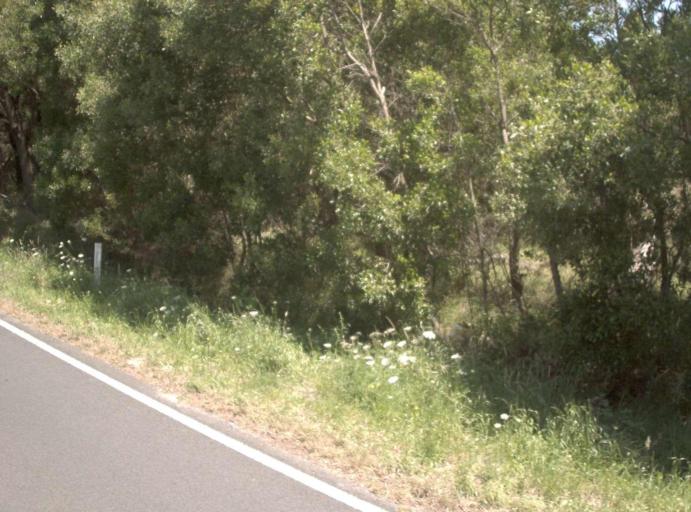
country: AU
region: Victoria
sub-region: Bass Coast
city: North Wonthaggi
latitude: -38.6550
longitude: 145.9341
